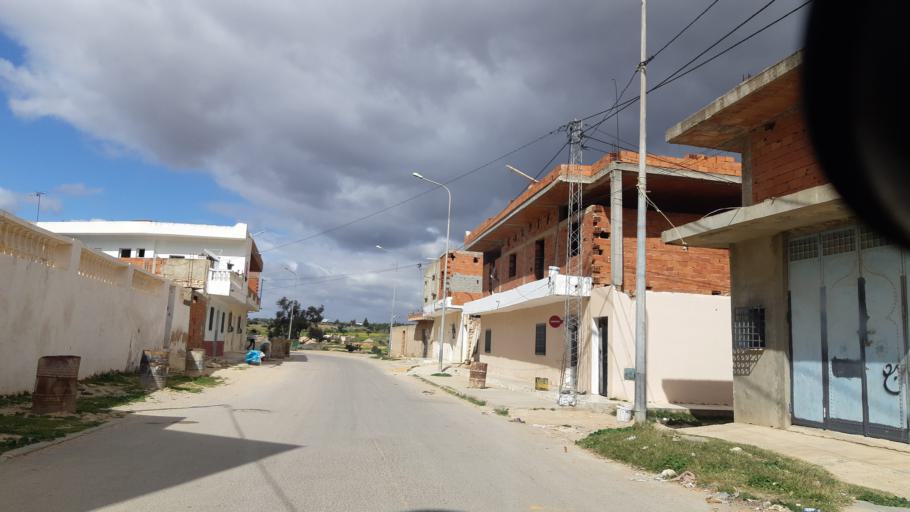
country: TN
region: Susah
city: Akouda
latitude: 35.8731
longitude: 10.5196
